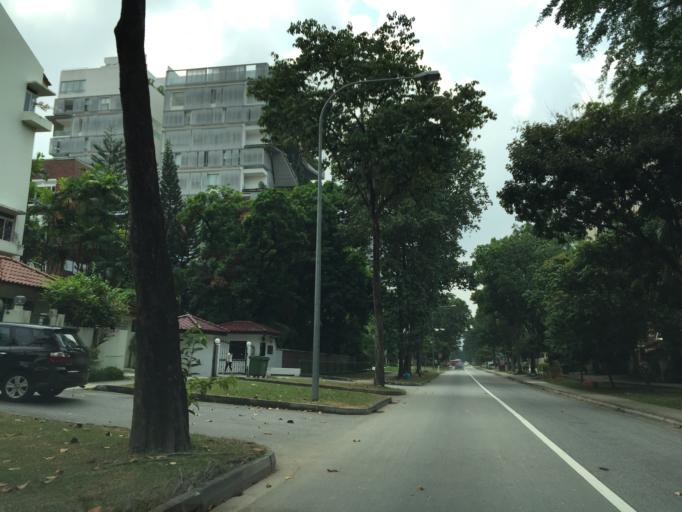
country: SG
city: Singapore
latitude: 1.3140
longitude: 103.8311
